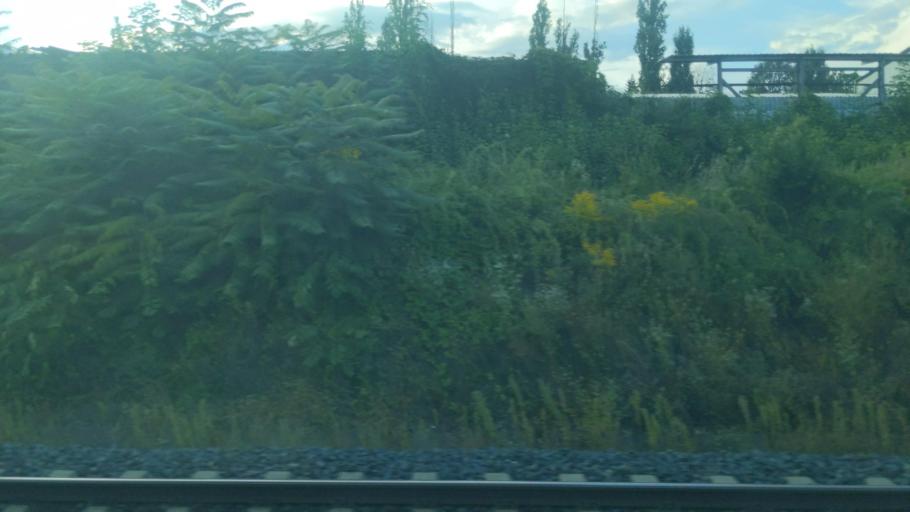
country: CZ
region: Praha
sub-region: Praha 8
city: Liben
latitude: 50.0994
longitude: 14.4759
